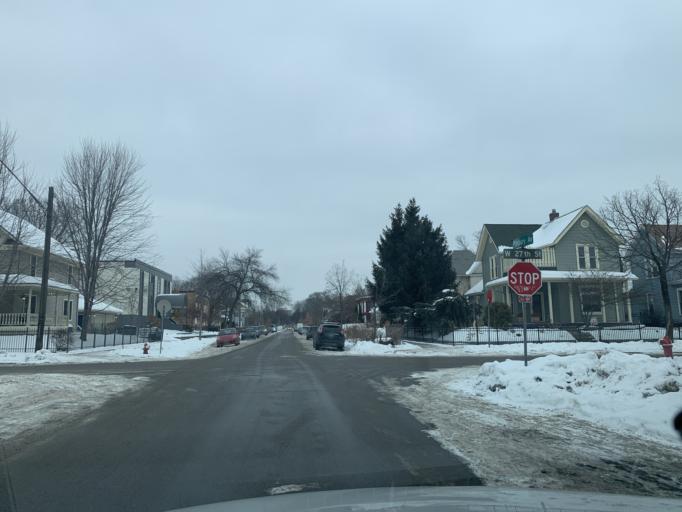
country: US
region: Minnesota
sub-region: Hennepin County
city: Minneapolis
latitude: 44.9539
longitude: -93.2814
